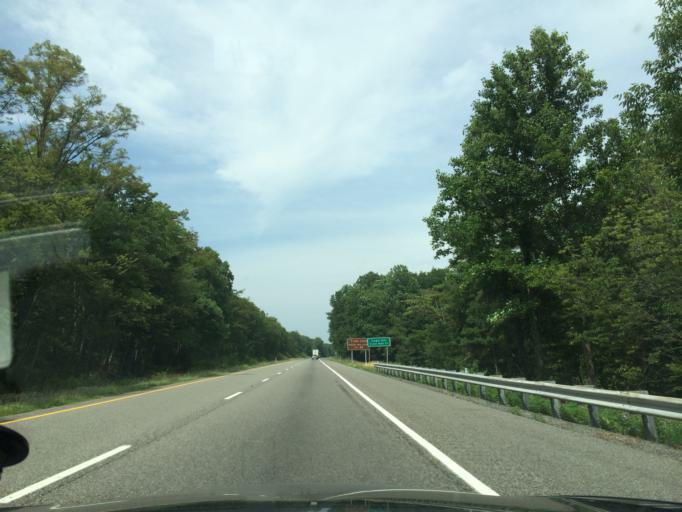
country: US
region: West Virginia
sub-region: Morgan County
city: Berkeley Springs
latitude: 39.6849
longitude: -78.4038
